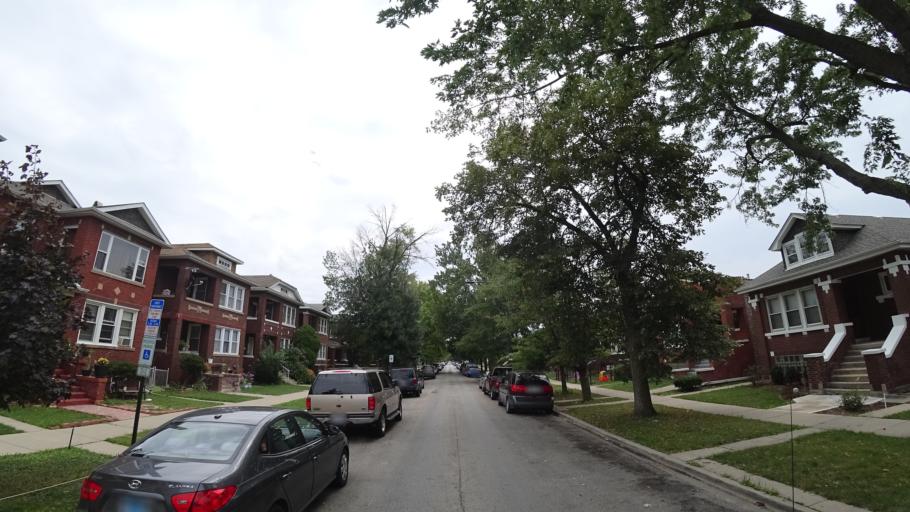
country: US
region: Illinois
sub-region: Cook County
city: Cicero
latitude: 41.8577
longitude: -87.7703
